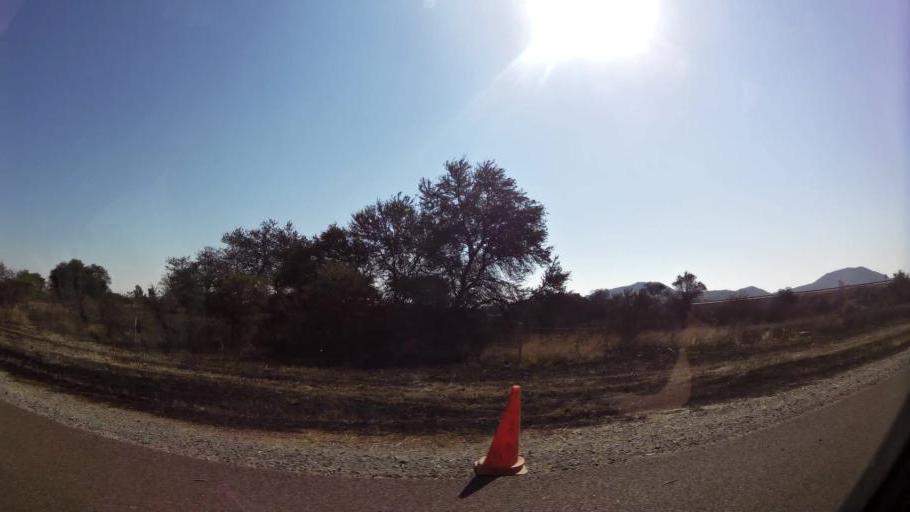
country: ZA
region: Gauteng
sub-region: City of Tshwane Metropolitan Municipality
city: Pretoria
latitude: -25.6469
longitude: 28.1492
